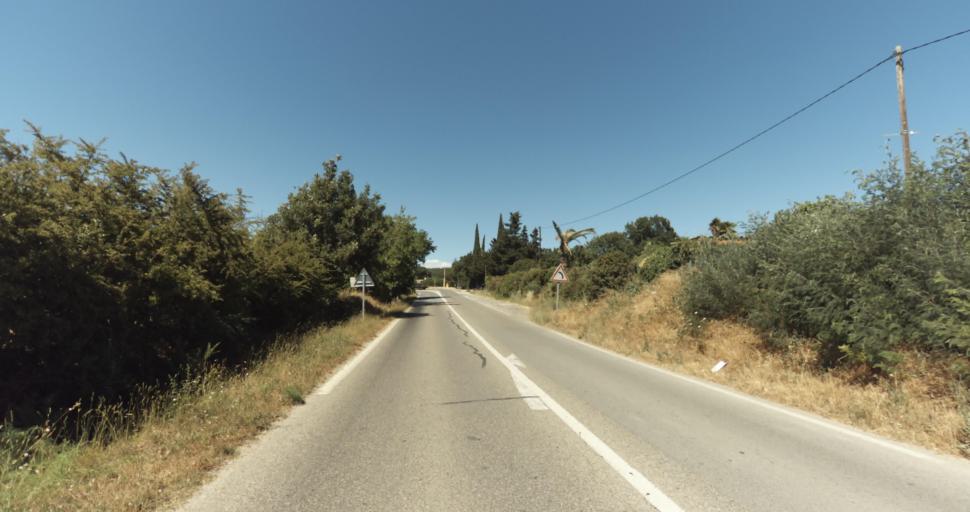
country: FR
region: Provence-Alpes-Cote d'Azur
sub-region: Departement du Var
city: Gassin
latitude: 43.2297
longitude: 6.5744
